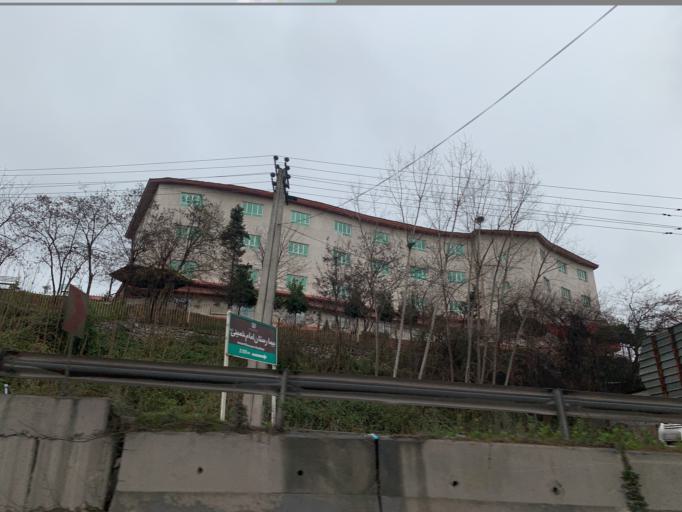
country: IR
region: Mazandaran
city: Amol
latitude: 36.4008
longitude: 52.3465
